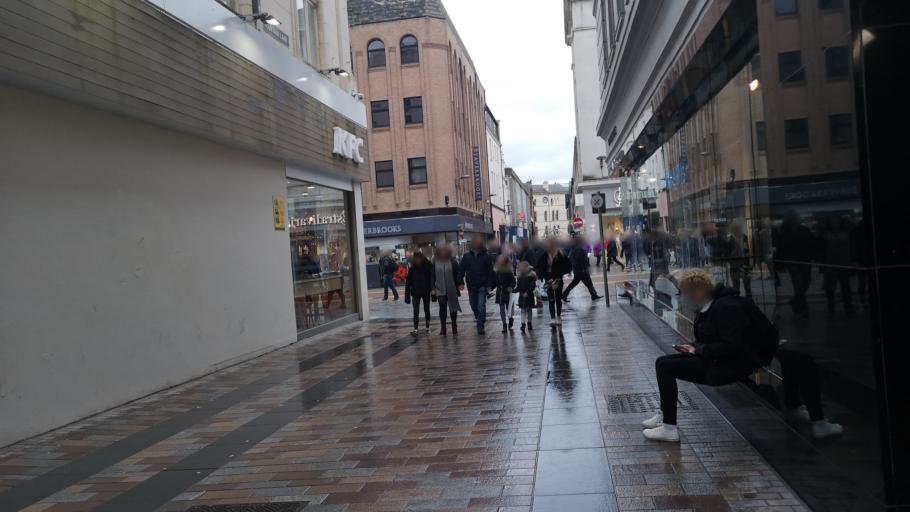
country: GB
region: Northern Ireland
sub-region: City of Belfast
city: Belfast
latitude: 54.5985
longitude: -5.9308
